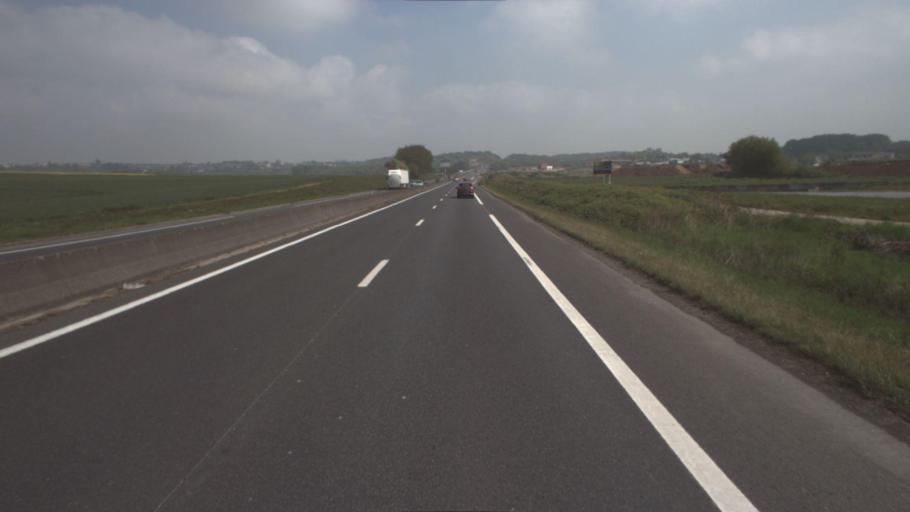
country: FR
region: Ile-de-France
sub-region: Departement de Seine-et-Marne
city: Longperrier
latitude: 49.0346
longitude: 2.6773
